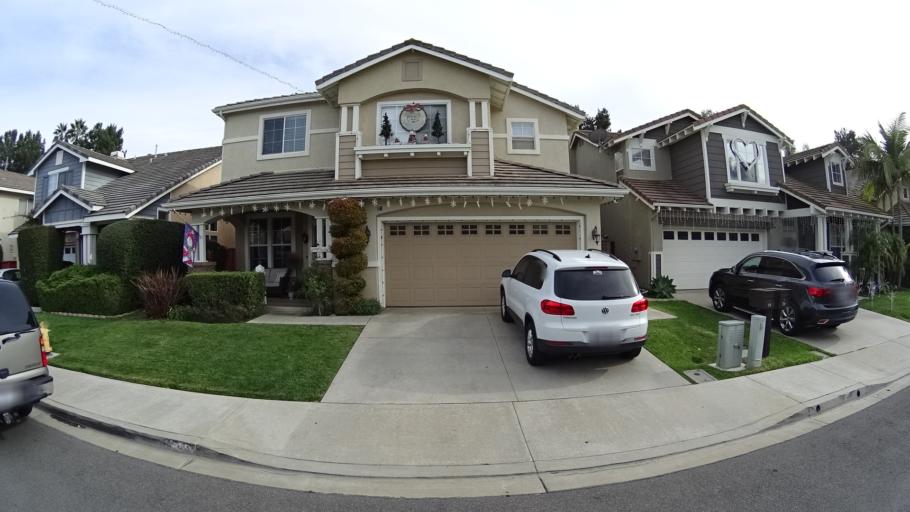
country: US
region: California
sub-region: Orange County
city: Aliso Viejo
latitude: 33.5861
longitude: -117.7422
